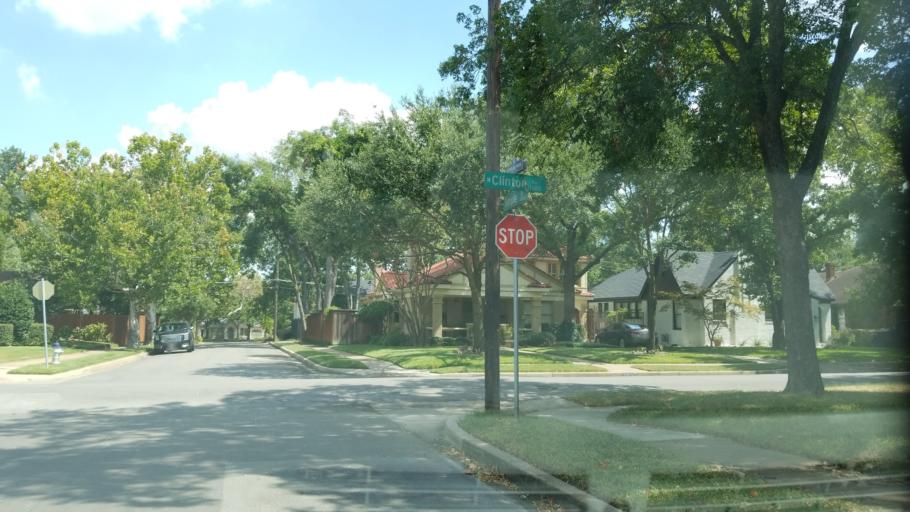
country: US
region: Texas
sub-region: Dallas County
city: Dallas
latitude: 32.7573
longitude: -96.8417
